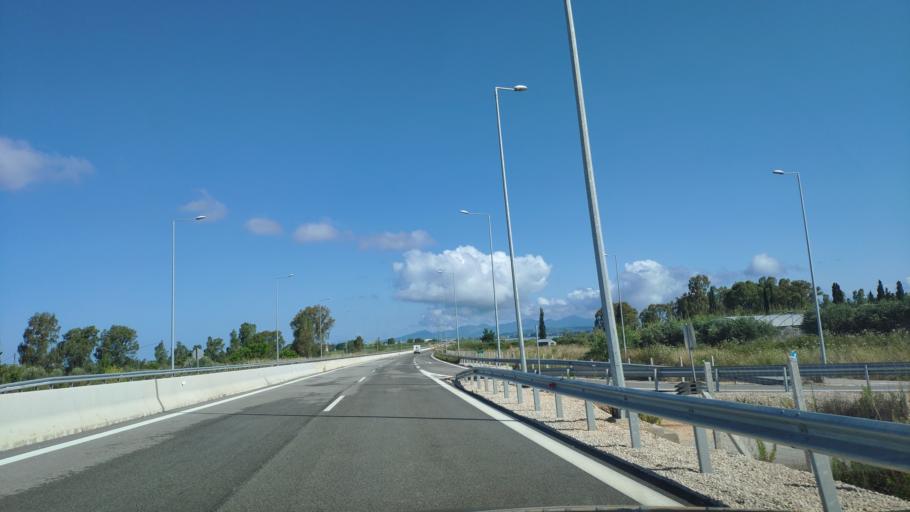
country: GR
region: Epirus
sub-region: Nomos Prevezis
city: Preveza
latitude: 38.9172
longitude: 20.7914
